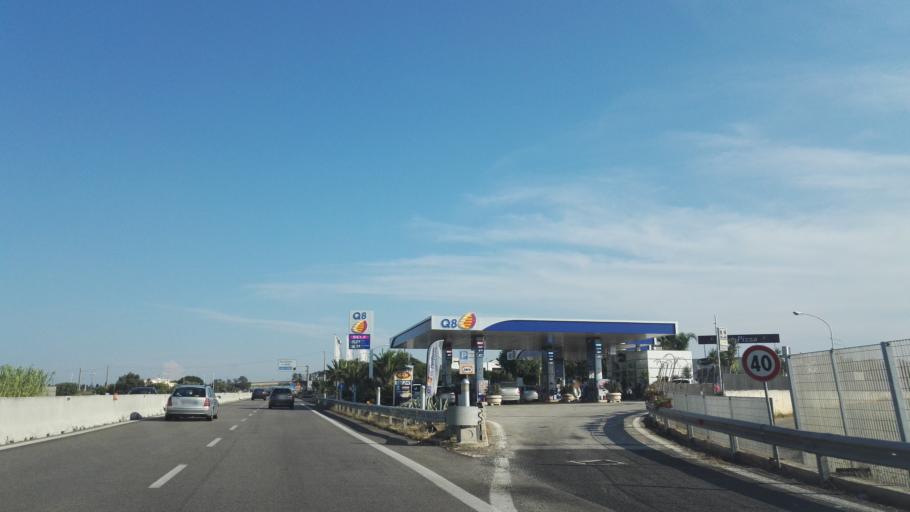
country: IT
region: Apulia
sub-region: Provincia di Bari
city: Polignano a Mare
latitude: 40.9953
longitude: 17.2042
